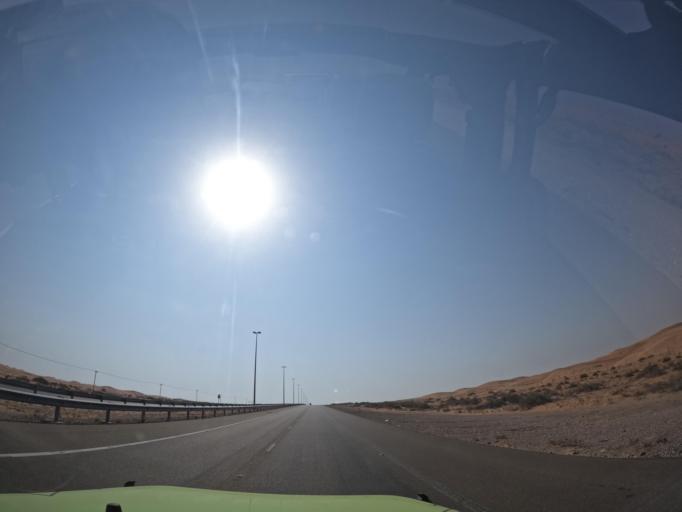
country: OM
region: Al Buraimi
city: Al Buraymi
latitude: 24.4496
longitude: 55.6539
